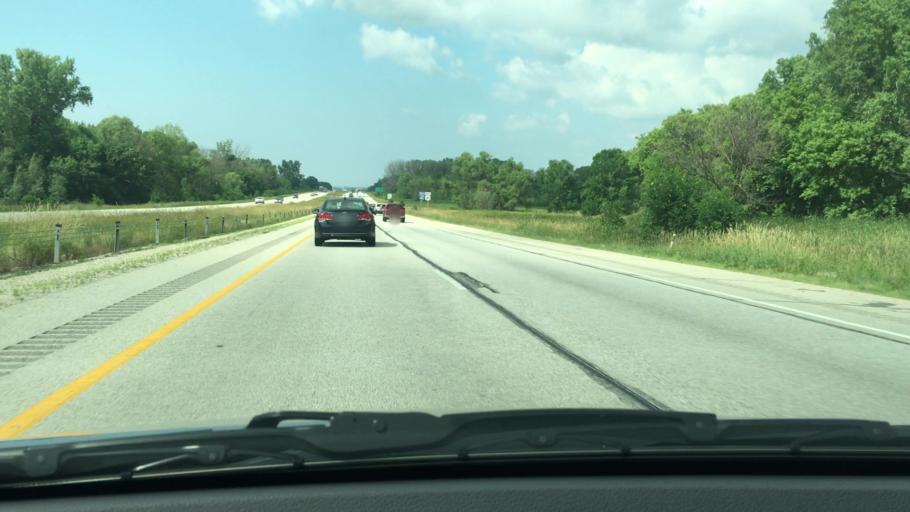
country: US
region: Wisconsin
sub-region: Fond du Lac County
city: Fond du Lac
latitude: 43.6986
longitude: -88.4421
